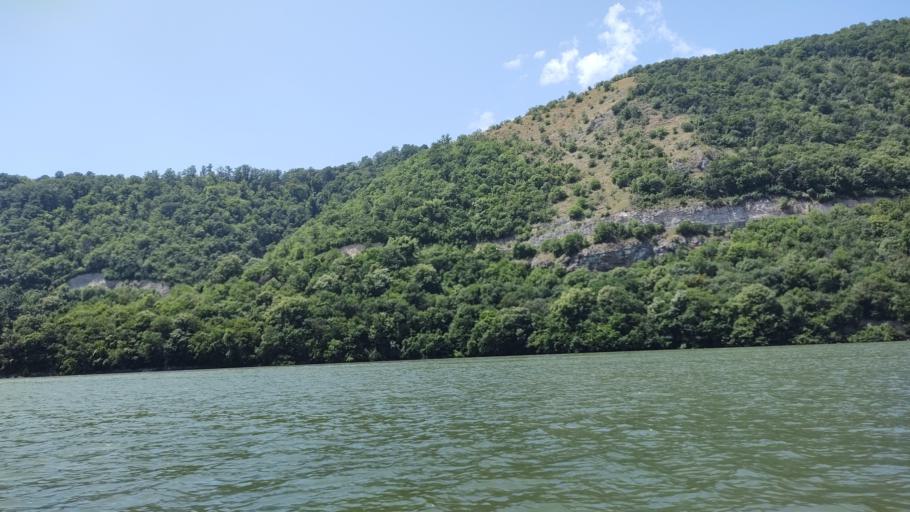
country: RO
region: Mehedinti
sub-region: Comuna Svinita
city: Svinita
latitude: 44.5555
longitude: 22.0303
